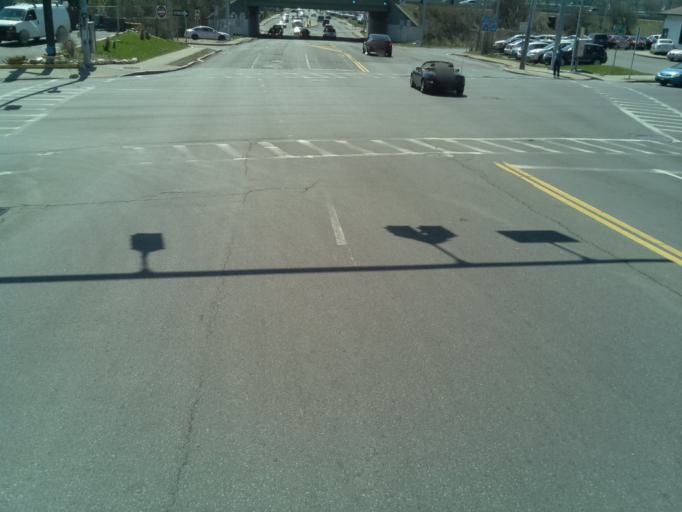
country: US
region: New York
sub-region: Onondaga County
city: Syracuse
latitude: 43.0545
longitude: -76.1218
